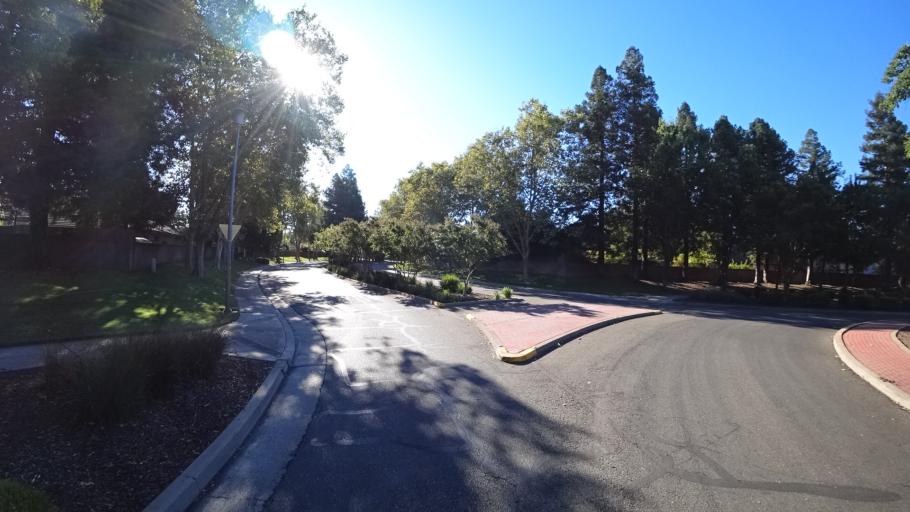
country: US
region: California
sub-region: Sacramento County
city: Elk Grove
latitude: 38.4274
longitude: -121.3768
